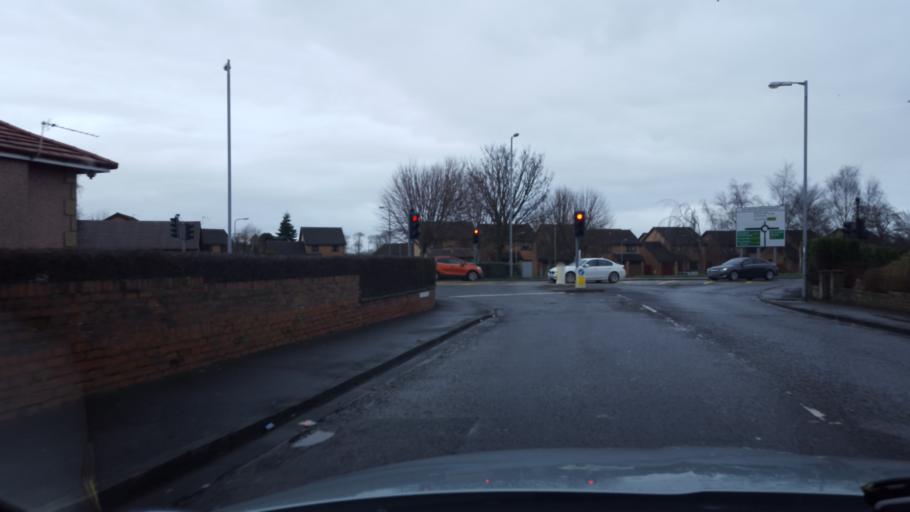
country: GB
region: Scotland
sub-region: South Ayrshire
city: Prestwick
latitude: 55.4551
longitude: -4.5991
